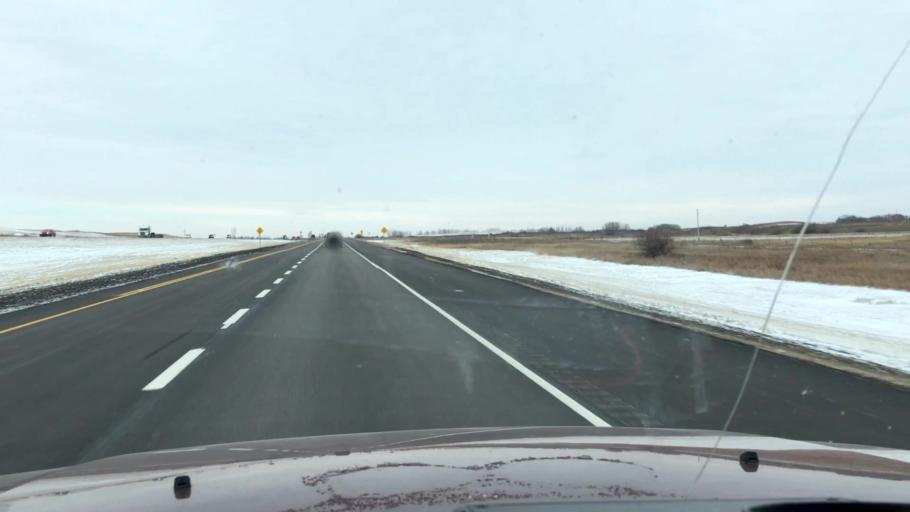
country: CA
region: Saskatchewan
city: Moose Jaw
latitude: 50.8649
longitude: -105.5959
